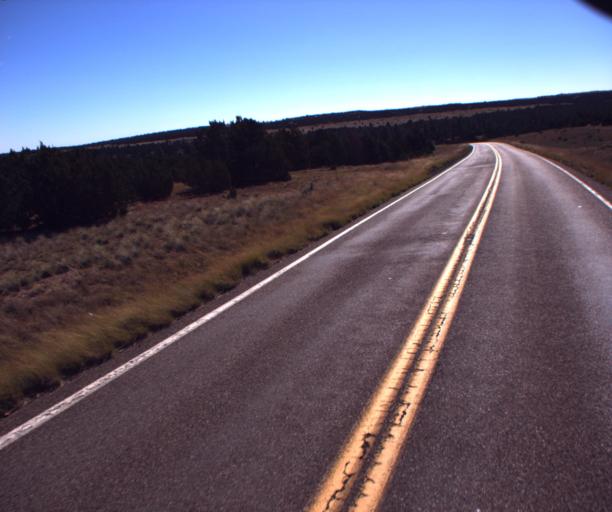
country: US
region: Arizona
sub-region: Navajo County
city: Heber-Overgaard
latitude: 34.4556
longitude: -110.4639
